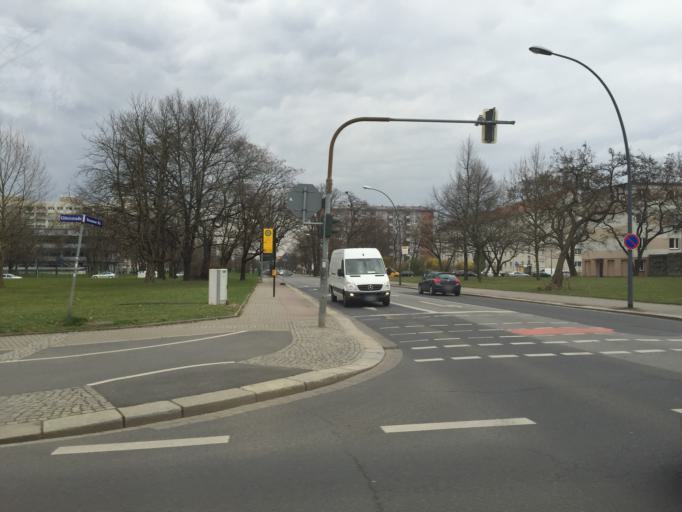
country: DE
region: Saxony
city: Dresden
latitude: 51.0499
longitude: 13.7572
